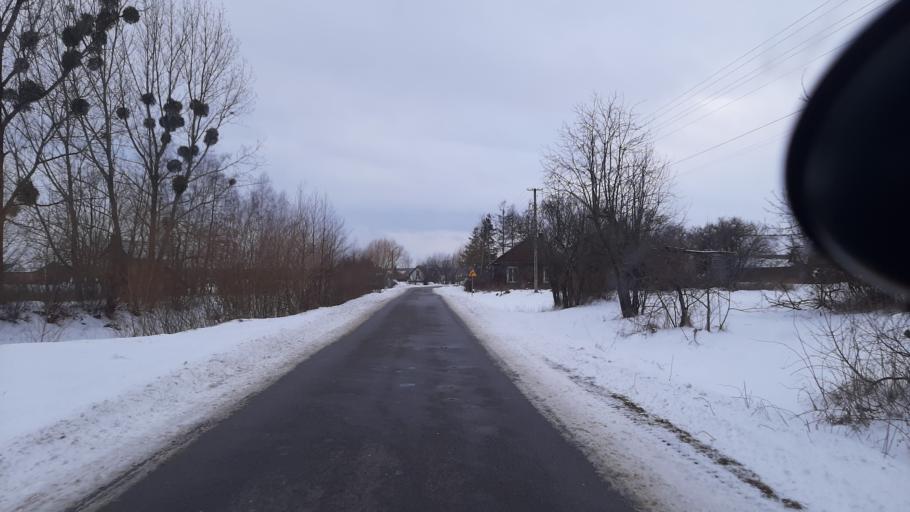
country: PL
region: Lublin Voivodeship
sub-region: Powiat lubartowski
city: Abramow
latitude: 51.4434
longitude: 22.2755
